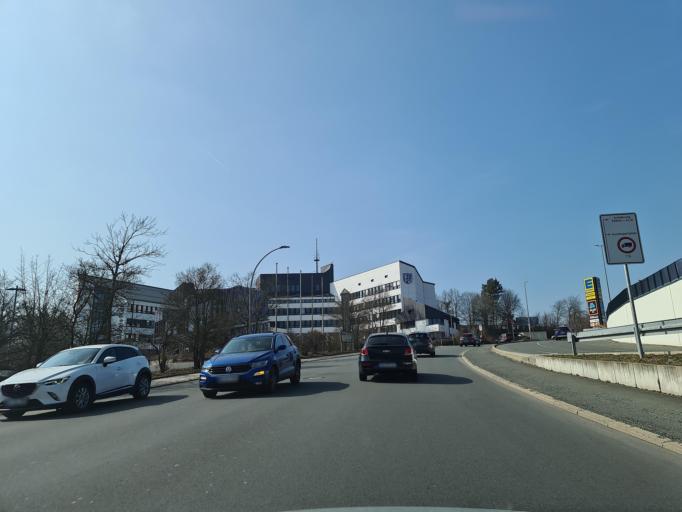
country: DE
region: Bavaria
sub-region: Upper Franconia
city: Oberkotzau
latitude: 50.2847
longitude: 11.9232
